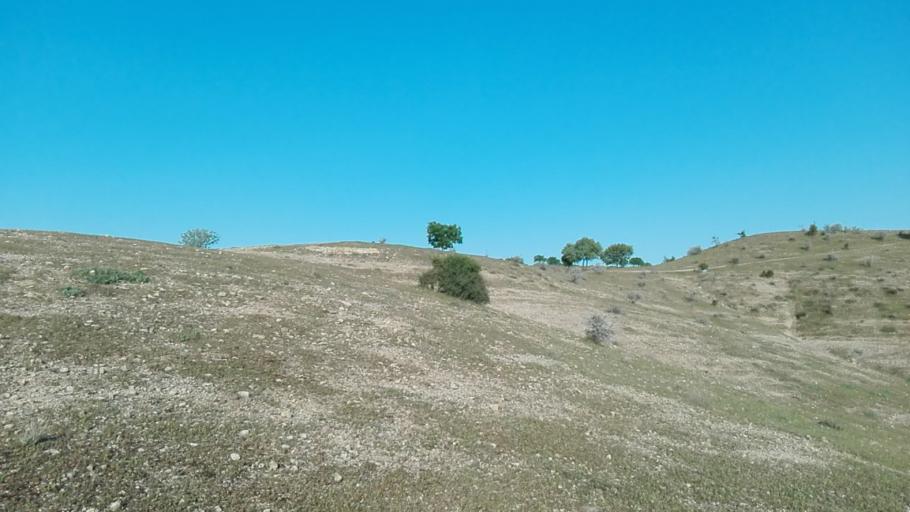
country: TR
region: Diyarbakir
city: Malabadi
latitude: 38.1776
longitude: 41.2171
